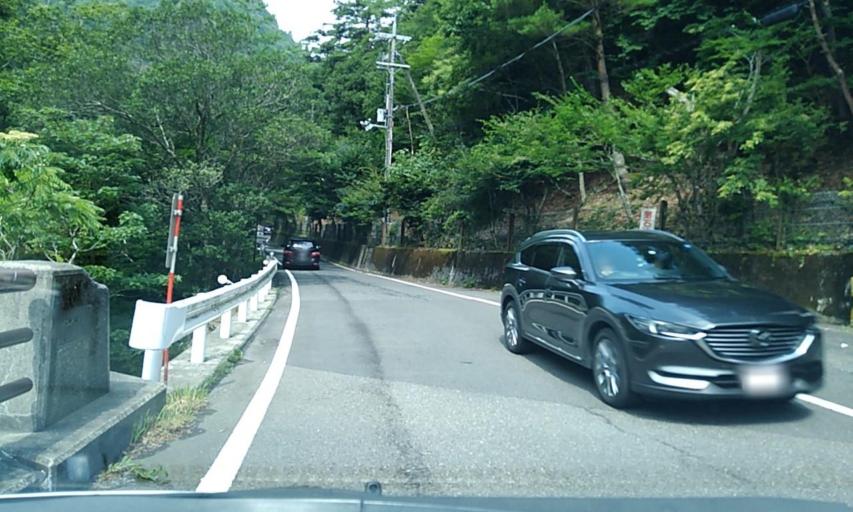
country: JP
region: Shiga Prefecture
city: Kitahama
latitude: 35.2697
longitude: 135.8633
